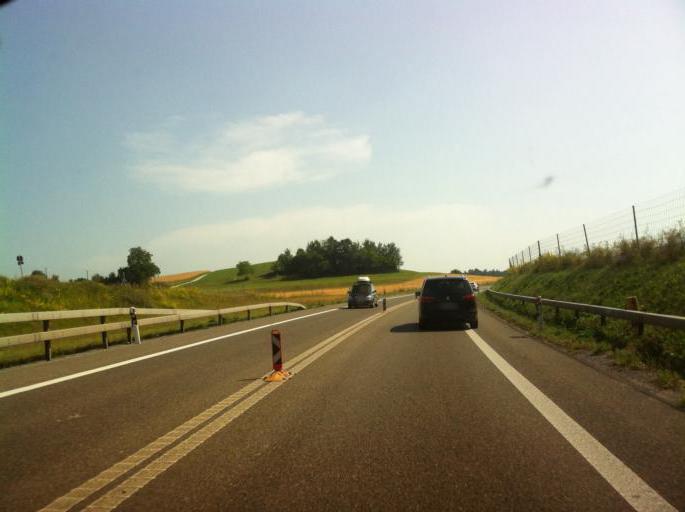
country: CH
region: Zurich
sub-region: Bezirk Andelfingen
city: Kleinandelfingen
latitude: 47.5901
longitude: 8.6907
